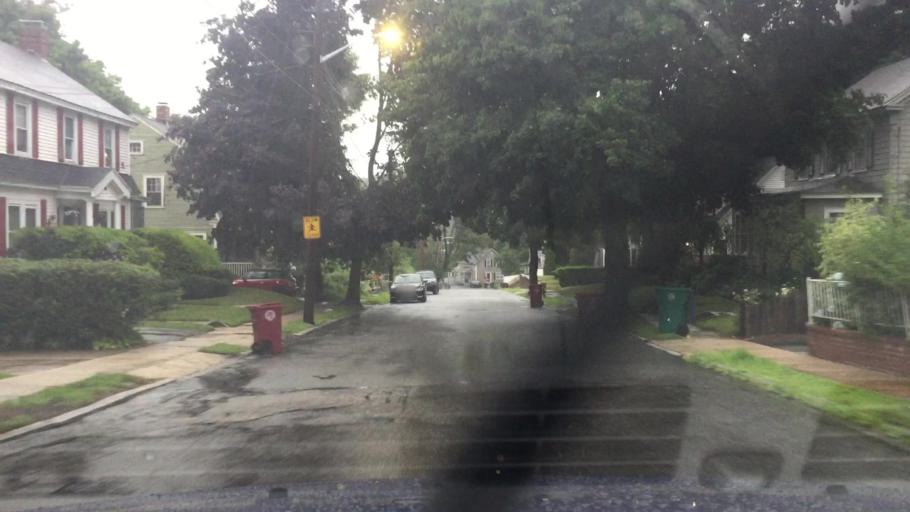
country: US
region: Massachusetts
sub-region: Middlesex County
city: Dracut
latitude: 42.6437
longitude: -71.2875
